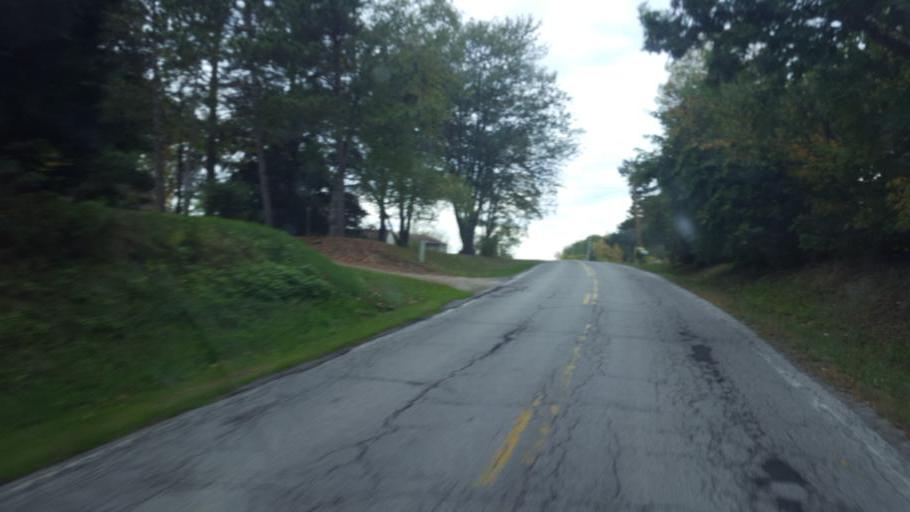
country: US
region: Ohio
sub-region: Huron County
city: Wakeman
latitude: 41.1961
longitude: -82.4206
